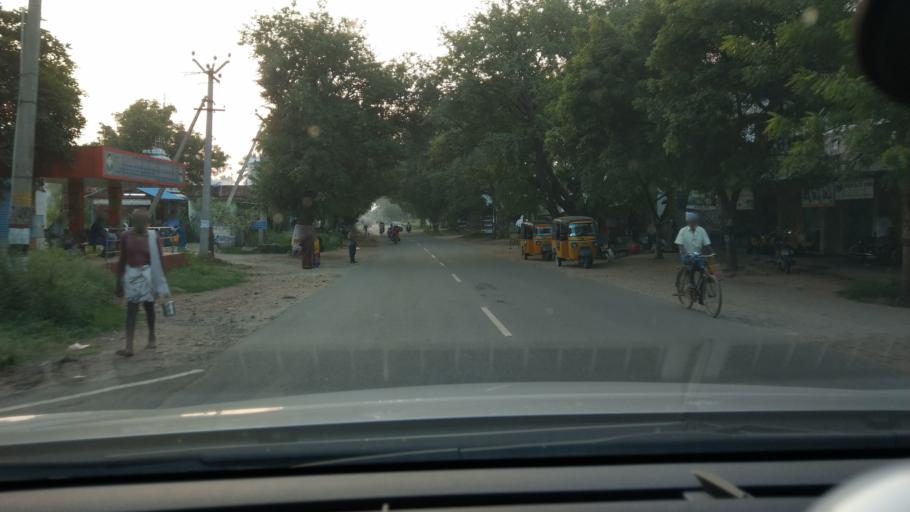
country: IN
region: Tamil Nadu
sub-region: Salem
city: Attur
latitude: 11.5993
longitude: 78.5791
